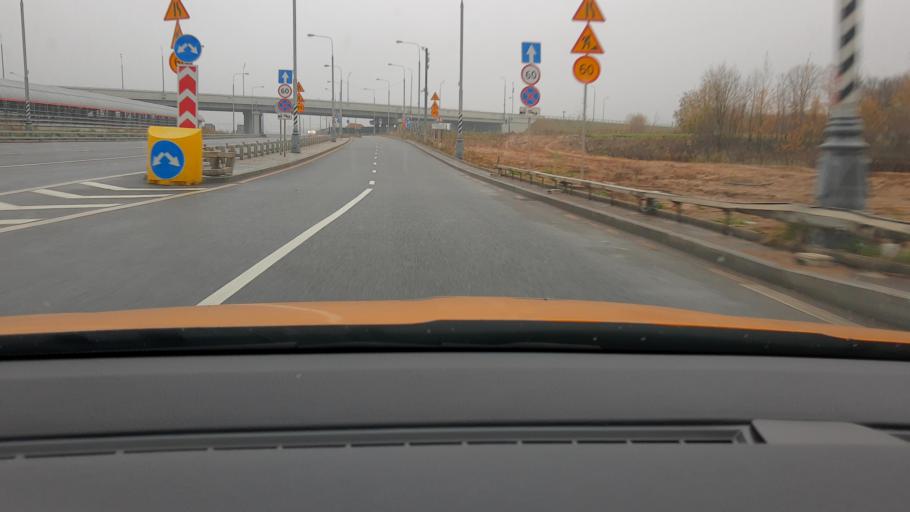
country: RU
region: Moskovskaya
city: Kommunarka
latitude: 55.5634
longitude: 37.4636
